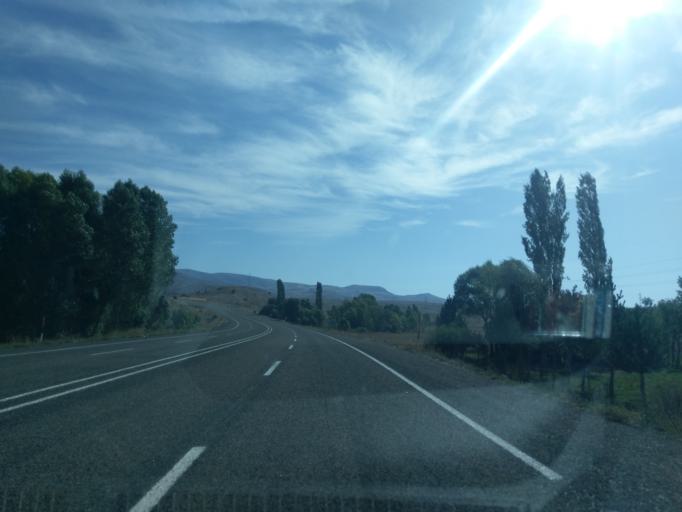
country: TR
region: Sivas
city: Imranli
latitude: 39.8353
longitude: 38.2640
